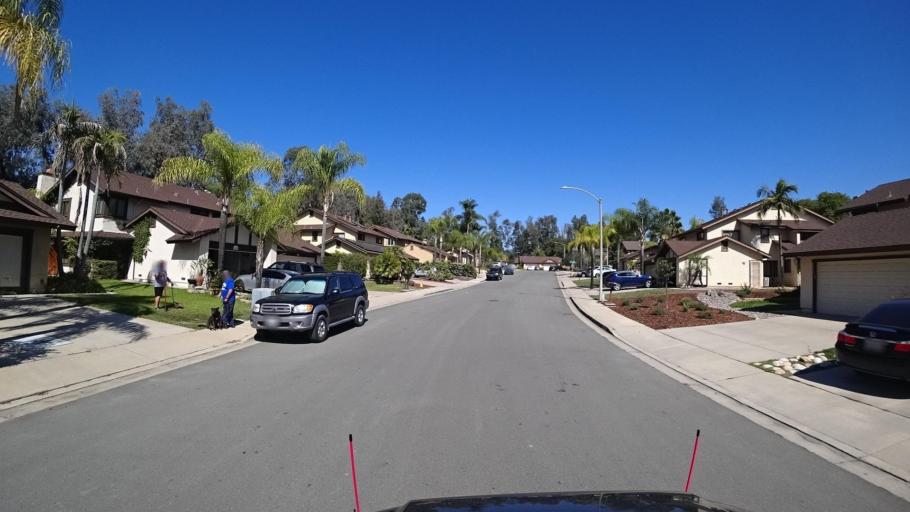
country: US
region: California
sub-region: San Diego County
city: Rancho San Diego
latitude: 32.7515
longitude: -116.9264
